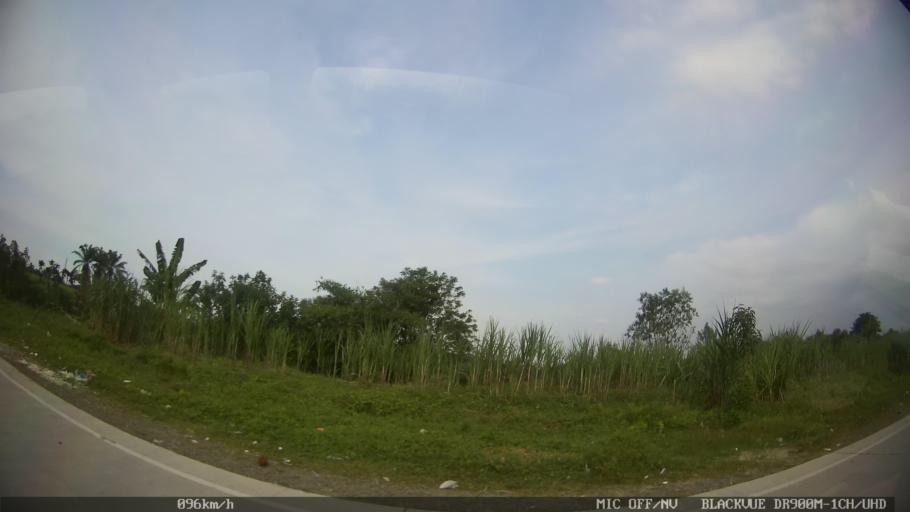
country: ID
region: North Sumatra
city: Binjai
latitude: 3.5979
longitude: 98.5329
